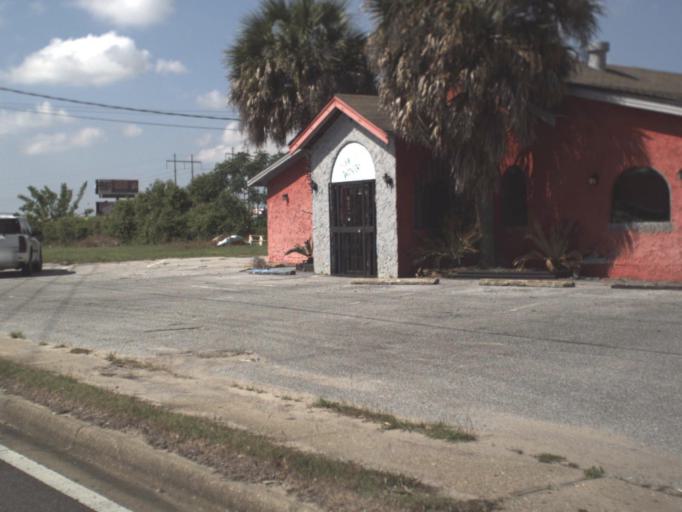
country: US
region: Florida
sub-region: Escambia County
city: Goulding
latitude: 30.4560
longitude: -87.2232
